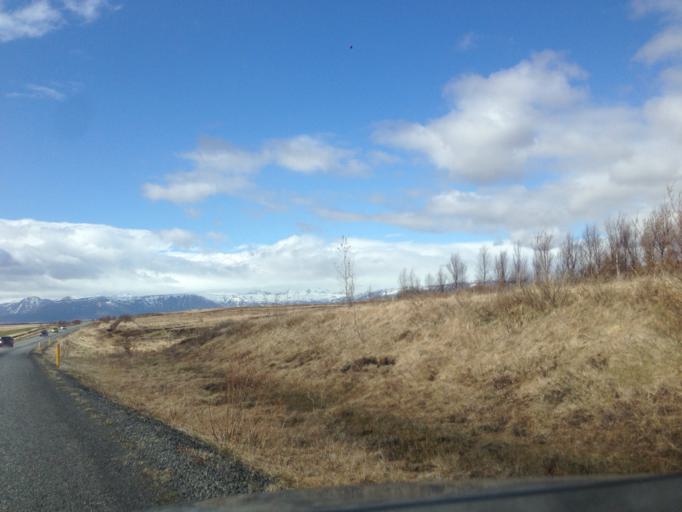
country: IS
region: South
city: Selfoss
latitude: 64.1322
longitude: -20.5317
